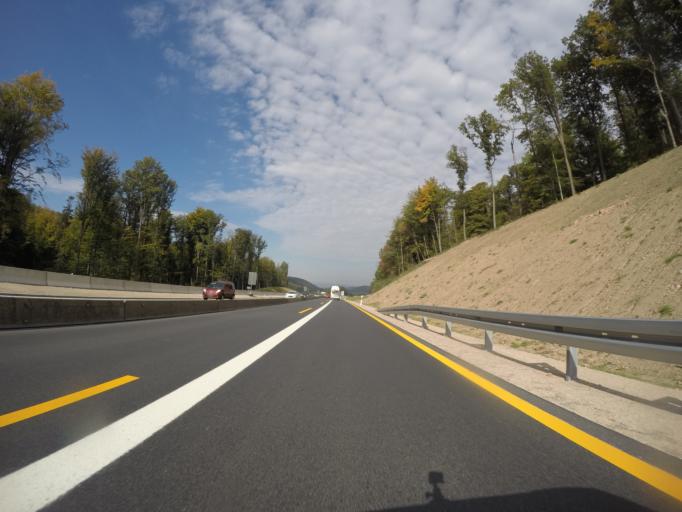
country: DE
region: Bavaria
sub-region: Regierungsbezirk Unterfranken
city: Weibersbrunn
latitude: 49.9433
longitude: 9.3397
